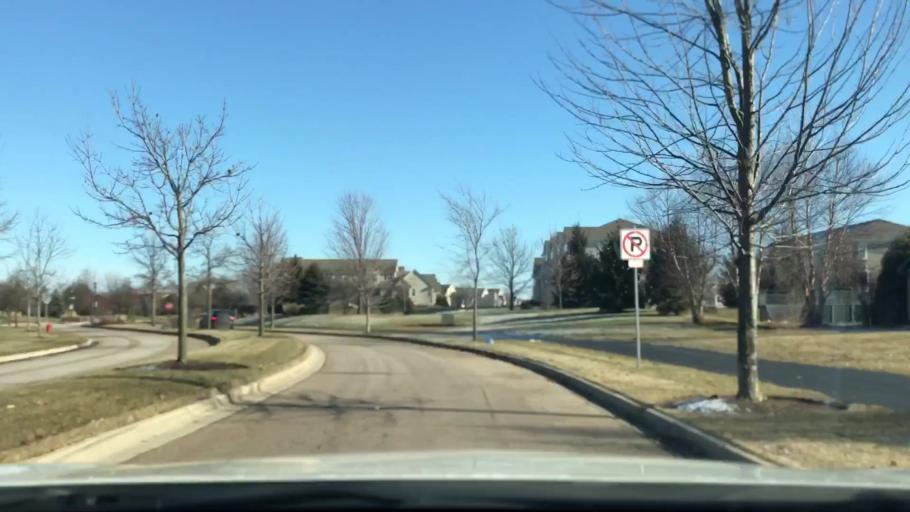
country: US
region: Illinois
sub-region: Kane County
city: Pingree Grove
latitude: 42.0855
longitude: -88.4484
